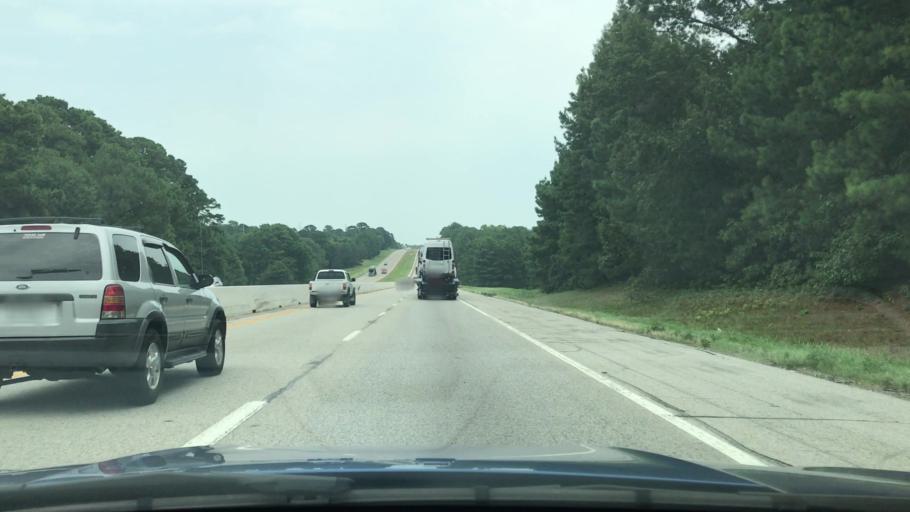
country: US
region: Texas
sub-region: Smith County
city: Hideaway
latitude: 32.4763
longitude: -95.4798
